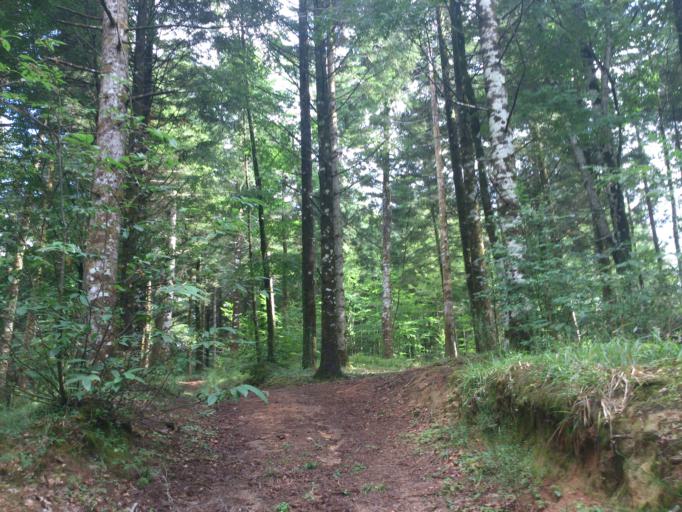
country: IT
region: Calabria
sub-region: Provincia di Vibo-Valentia
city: Serra San Bruno
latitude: 38.5477
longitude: 16.3102
